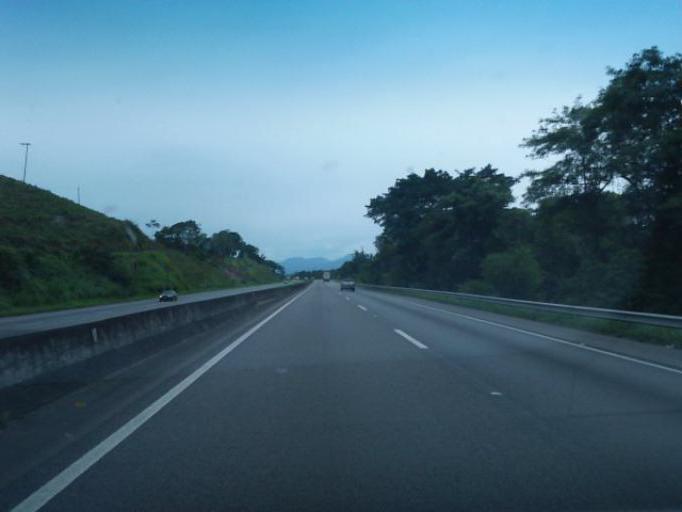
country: BR
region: Sao Paulo
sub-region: Jacupiranga
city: Jacupiranga
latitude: -24.6626
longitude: -47.9717
